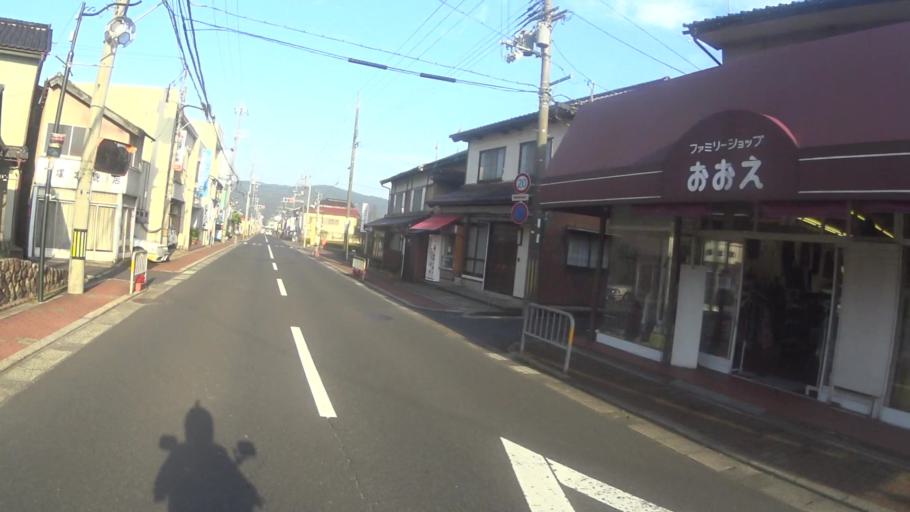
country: JP
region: Kyoto
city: Miyazu
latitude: 35.6252
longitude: 135.0597
